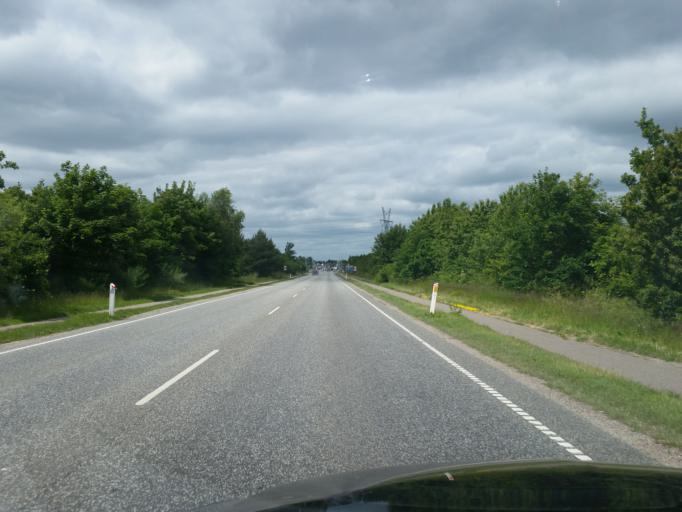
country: DK
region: Central Jutland
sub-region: Horsens Kommune
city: Horsens
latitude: 55.8811
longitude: 9.7968
